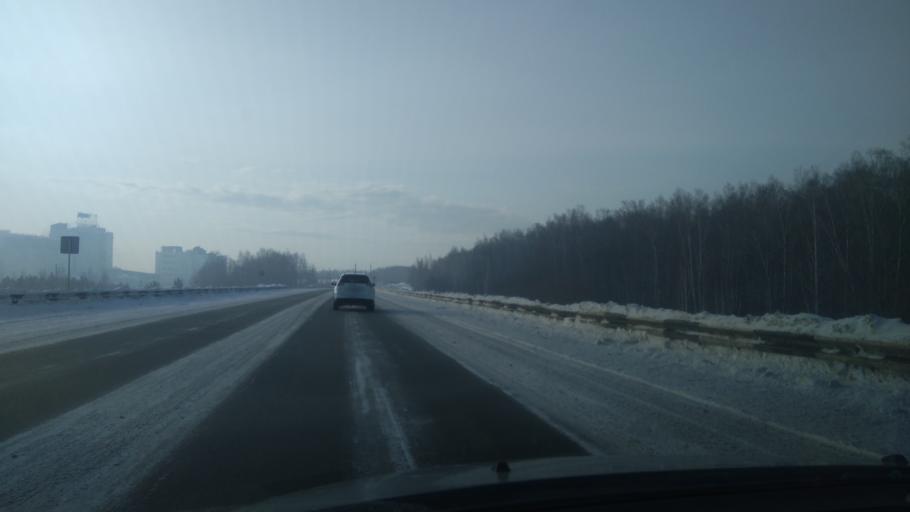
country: RU
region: Sverdlovsk
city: Bogdanovich
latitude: 56.8116
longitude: 62.0414
